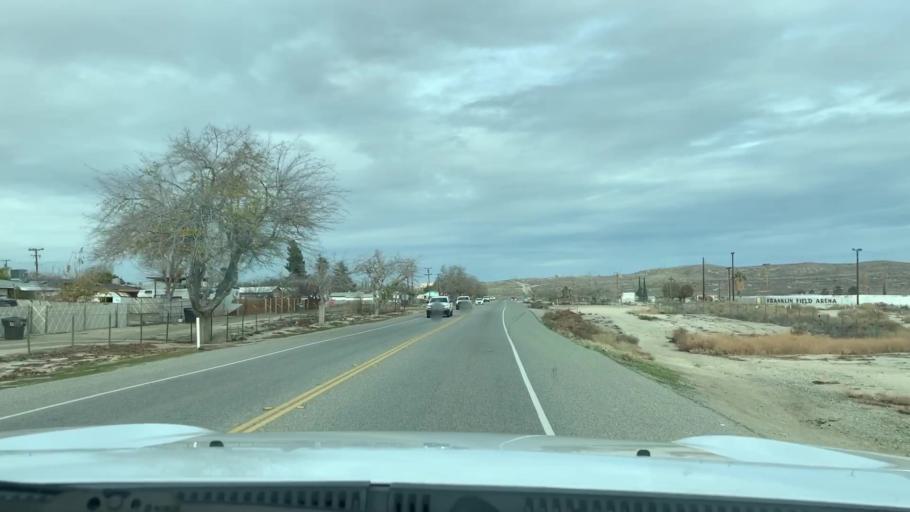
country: US
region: California
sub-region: Kern County
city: Ford City
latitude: 35.1502
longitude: -119.4479
